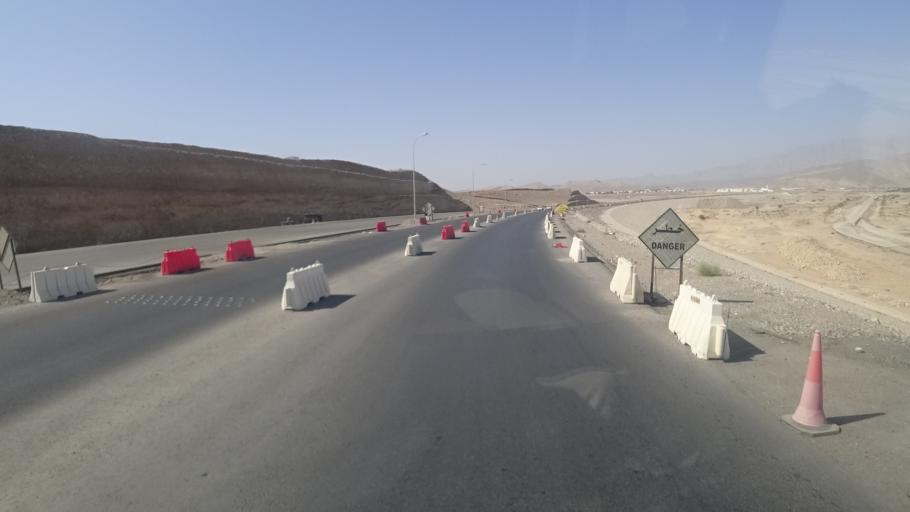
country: OM
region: Ash Sharqiyah
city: Sur
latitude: 22.5206
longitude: 59.4629
